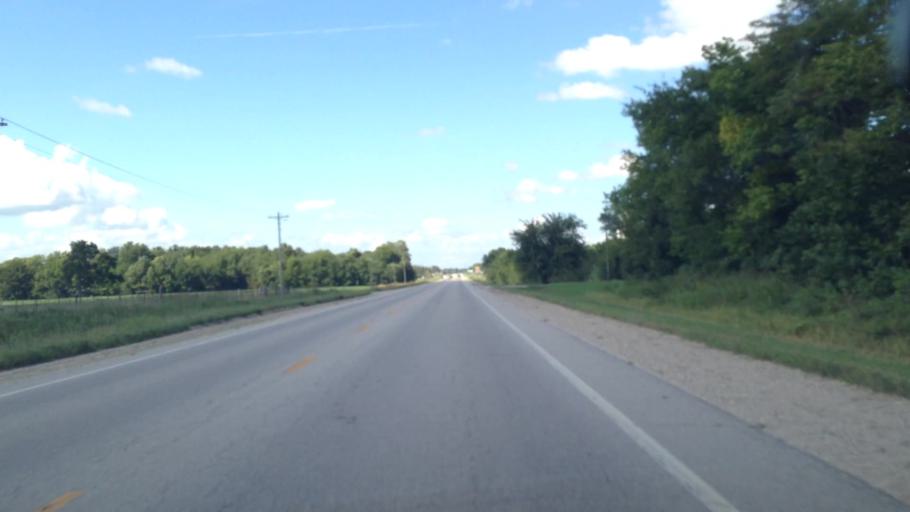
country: US
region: Kansas
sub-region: Neosho County
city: Erie
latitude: 37.5103
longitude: -95.2691
